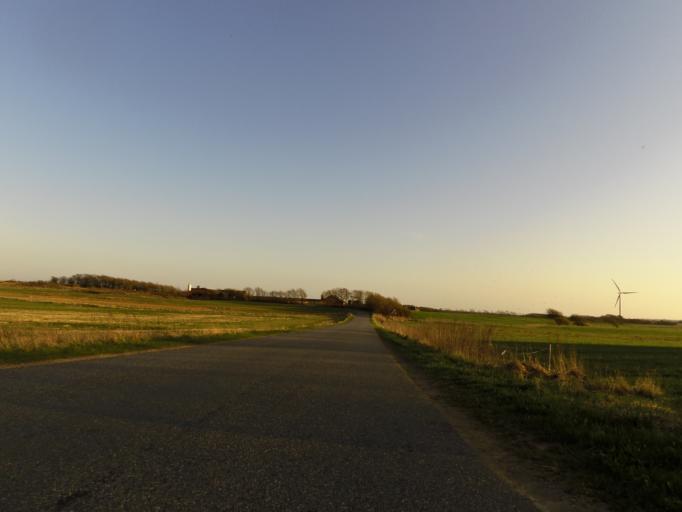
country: DK
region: Central Jutland
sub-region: Holstebro Kommune
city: Vinderup
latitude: 56.5165
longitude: 8.7947
